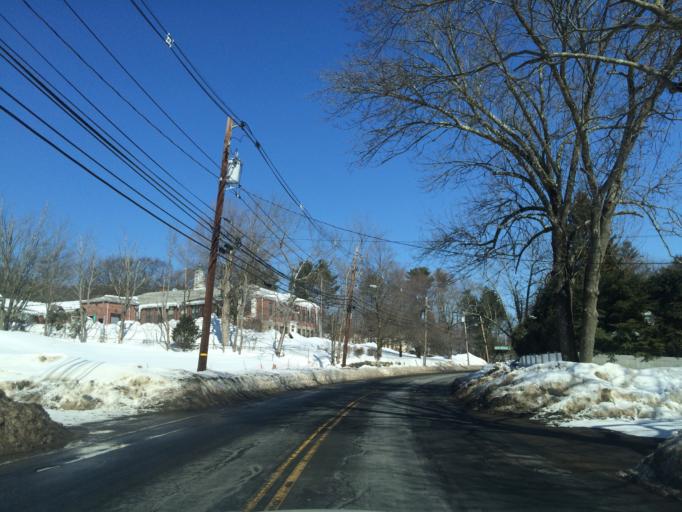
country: US
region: Massachusetts
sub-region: Norfolk County
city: Needham
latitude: 42.2862
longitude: -71.2526
